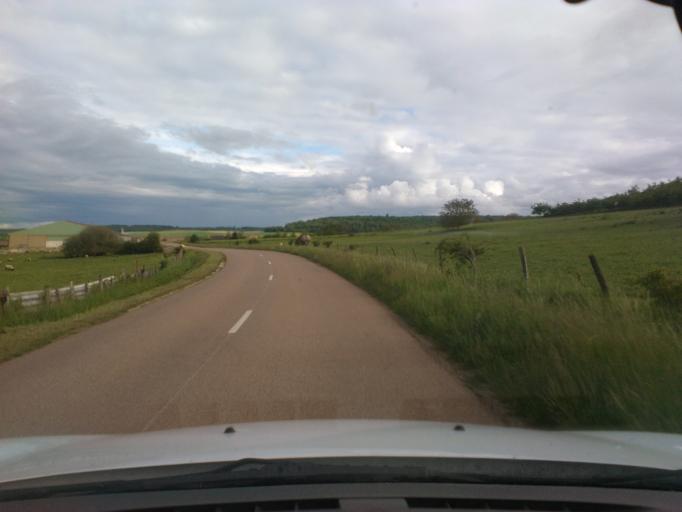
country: FR
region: Lorraine
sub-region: Departement des Vosges
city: Mirecourt
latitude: 48.3188
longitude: 6.0472
